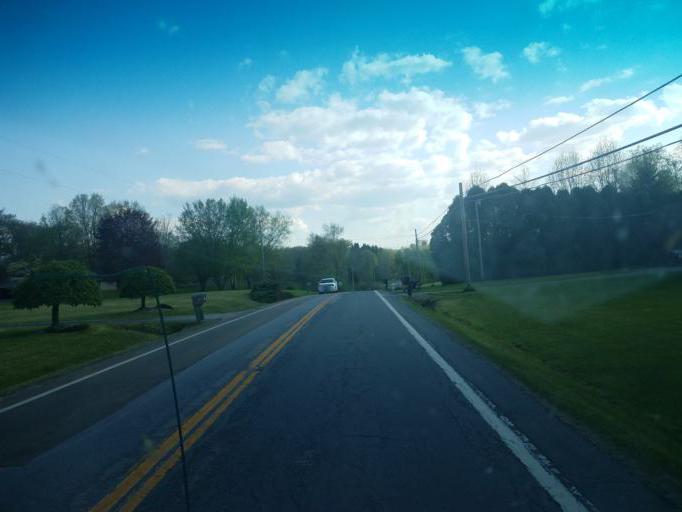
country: US
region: Ohio
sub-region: Wayne County
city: Wooster
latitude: 40.7329
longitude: -81.9389
